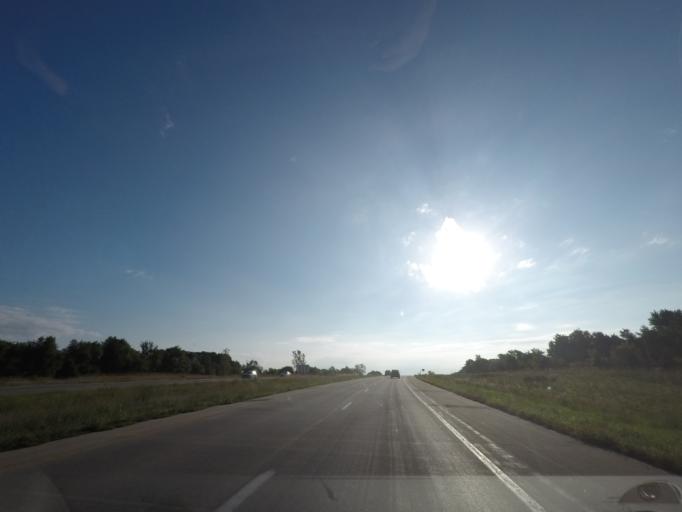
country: US
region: Iowa
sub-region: Warren County
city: Carlisle
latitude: 41.5117
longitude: -93.5466
